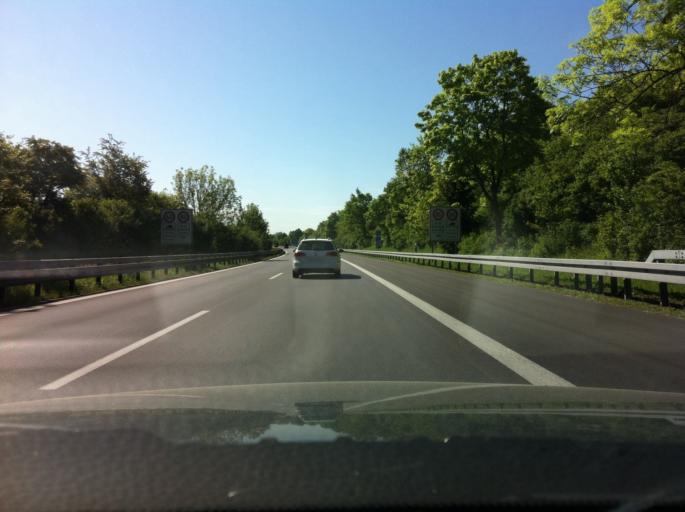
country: DE
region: Bavaria
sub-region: Upper Bavaria
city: Oberhaching
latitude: 48.0409
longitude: 11.5994
